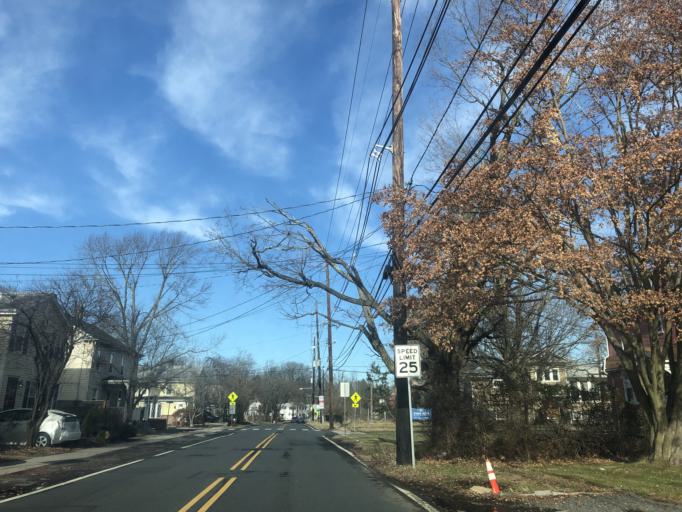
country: US
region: New Jersey
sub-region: Somerset County
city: Kingston
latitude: 40.3766
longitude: -74.6141
